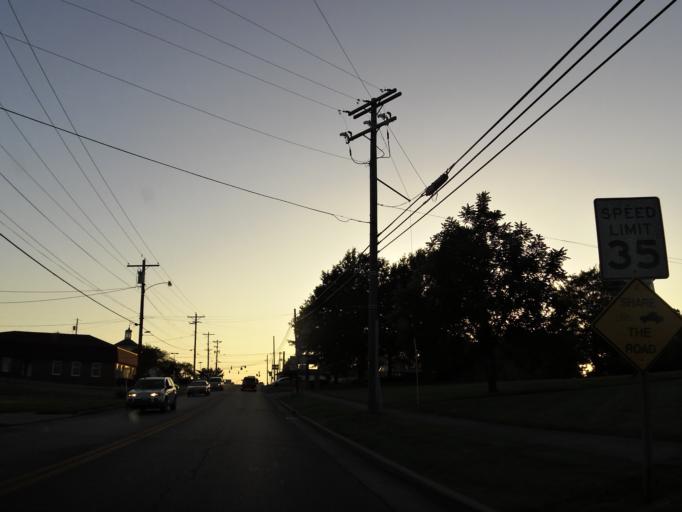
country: US
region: Kentucky
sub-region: Madison County
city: Berea
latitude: 37.5681
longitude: -84.3036
